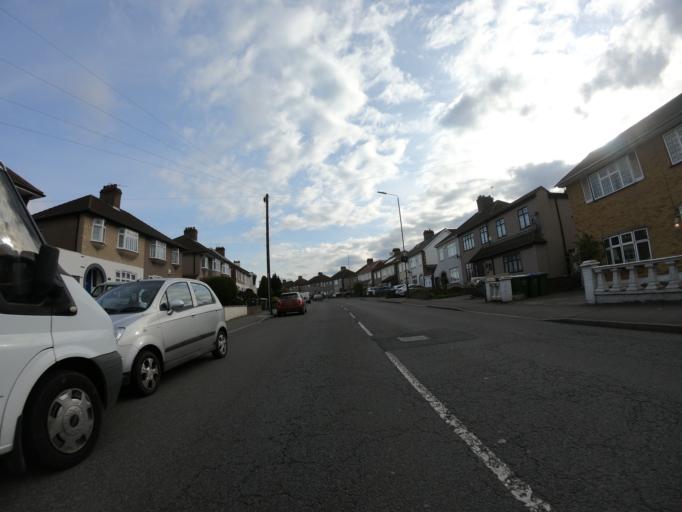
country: GB
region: England
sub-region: Greater London
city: Bexleyheath
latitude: 51.4763
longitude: 0.1449
